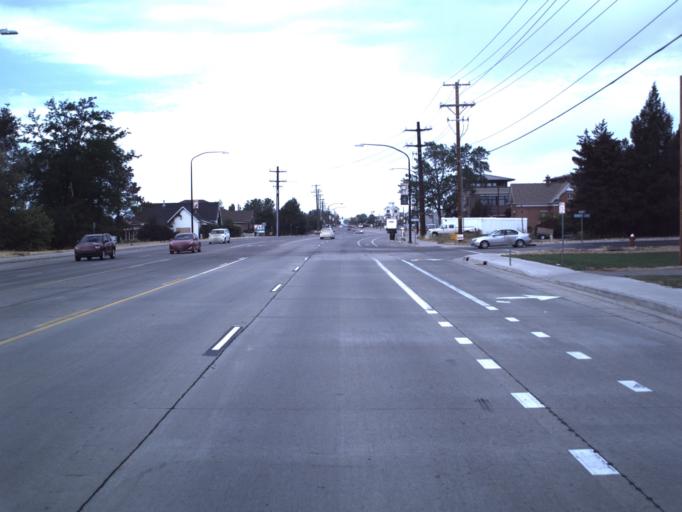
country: US
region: Utah
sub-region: Davis County
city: Syracuse
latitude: 41.0891
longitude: -112.0588
